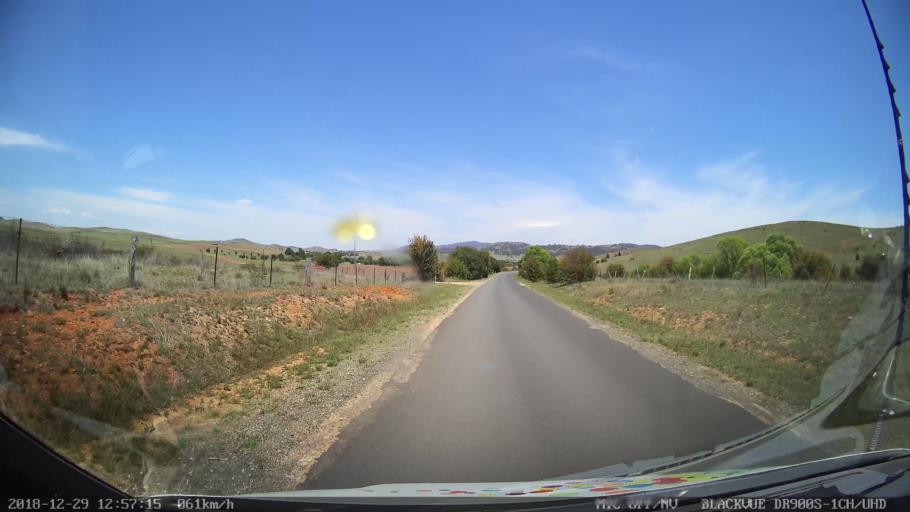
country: AU
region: Australian Capital Territory
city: Macarthur
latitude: -35.7068
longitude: 149.1788
